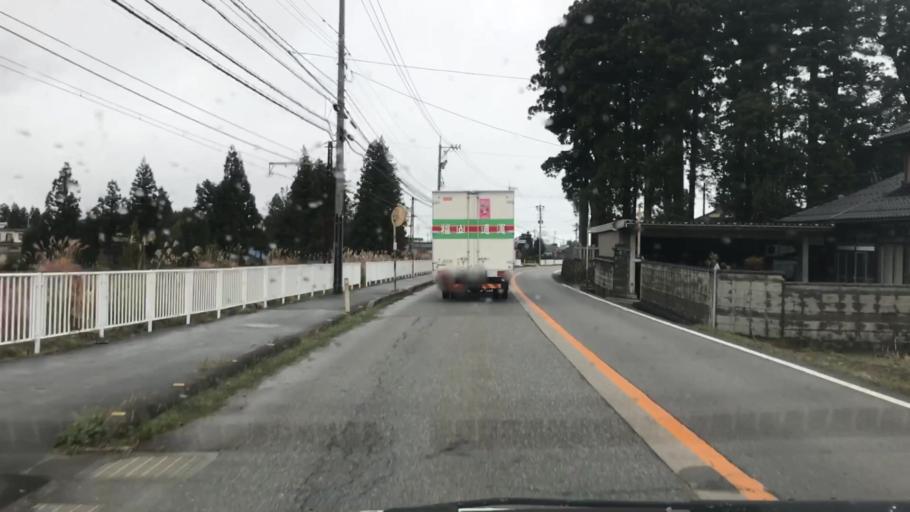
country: JP
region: Toyama
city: Kamiichi
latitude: 36.6037
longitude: 137.3208
